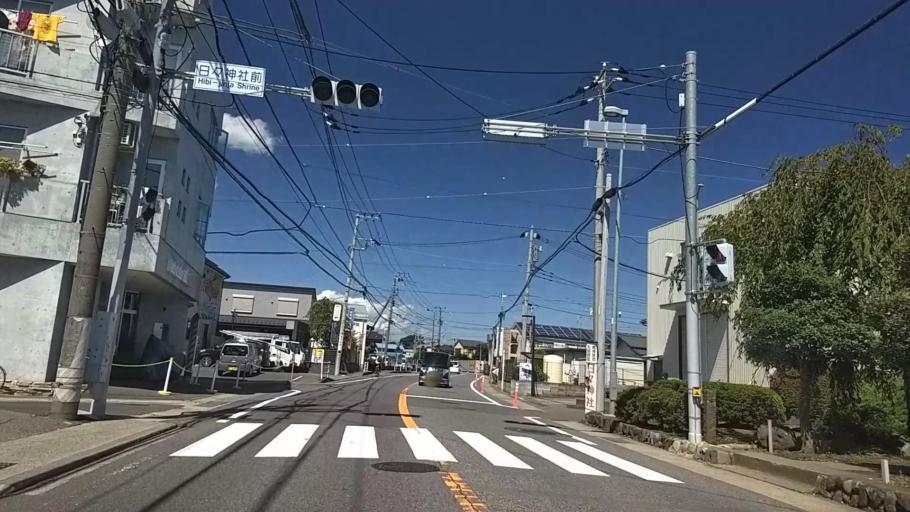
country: JP
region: Tokyo
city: Hachioji
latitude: 35.5685
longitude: 139.3218
